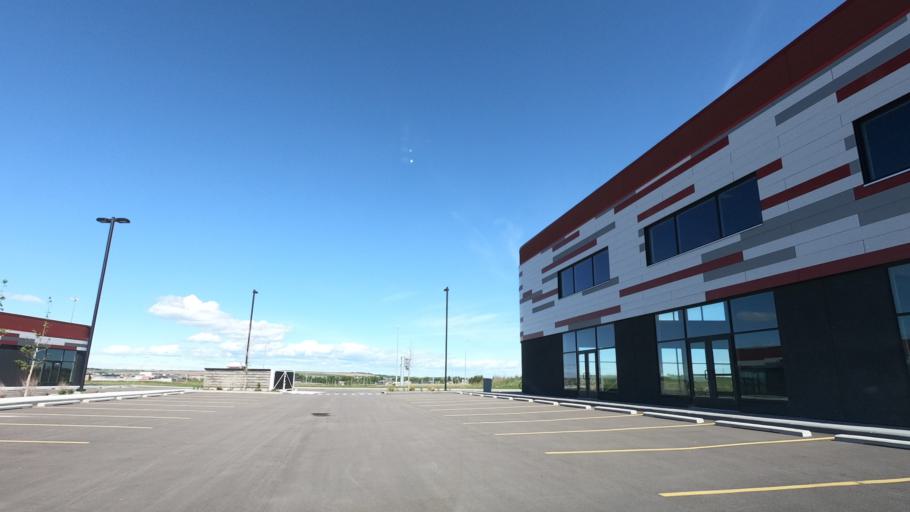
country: CA
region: Alberta
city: Airdrie
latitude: 51.2684
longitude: -113.9984
